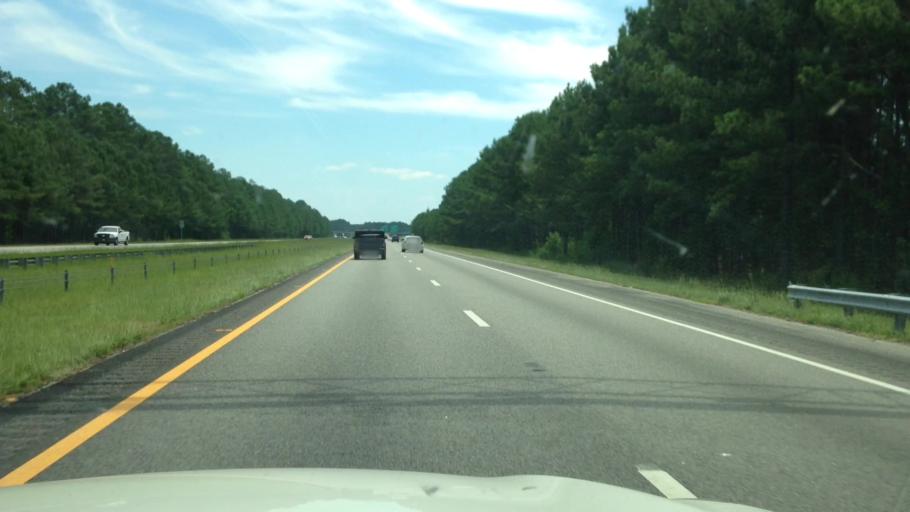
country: US
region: South Carolina
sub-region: Florence County
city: Florence
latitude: 34.2002
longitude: -79.8605
